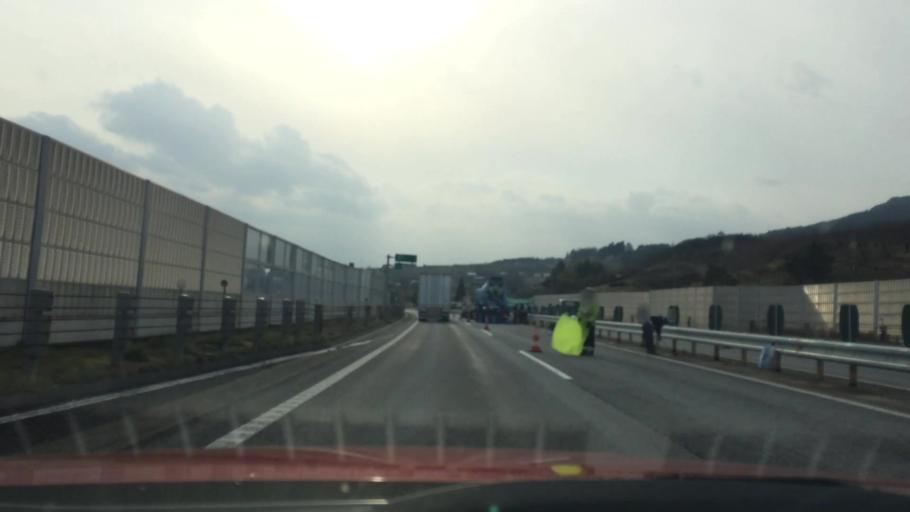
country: JP
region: Nagano
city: Iida
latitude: 35.5526
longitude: 137.8497
